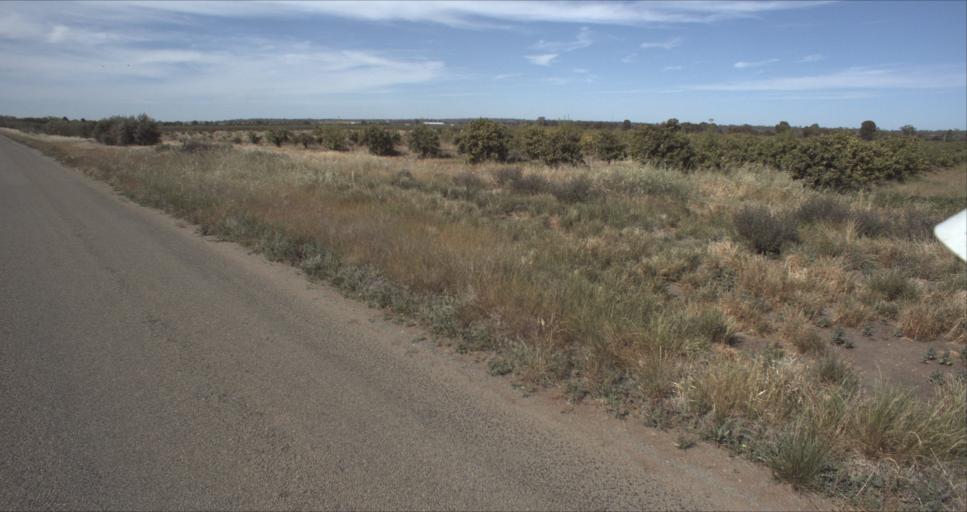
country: AU
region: New South Wales
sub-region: Leeton
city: Leeton
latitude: -34.5677
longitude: 146.4725
